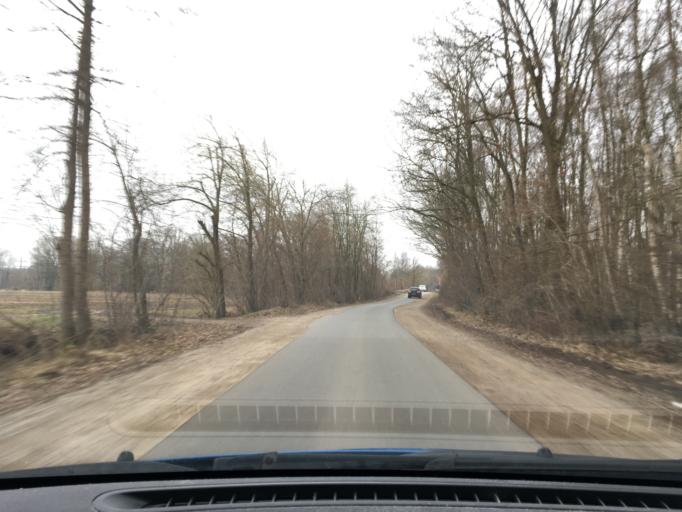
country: DE
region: Lower Saxony
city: Vogelsen
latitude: 53.2841
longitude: 10.3463
